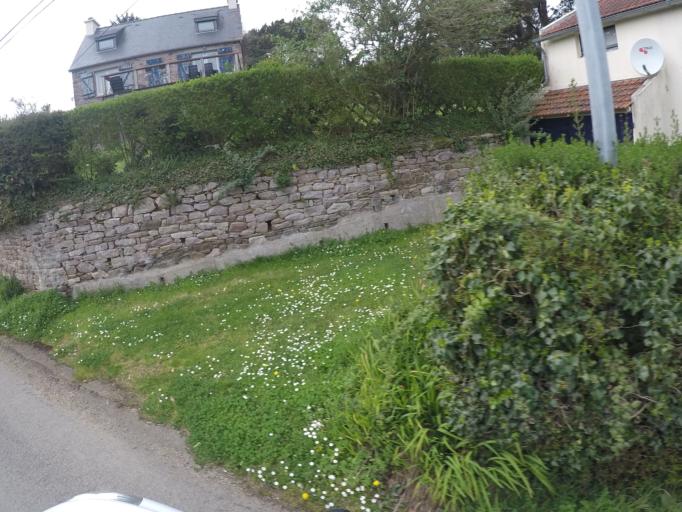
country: FR
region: Brittany
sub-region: Departement des Cotes-d'Armor
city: Plouezec
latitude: 48.7224
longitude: -2.9514
